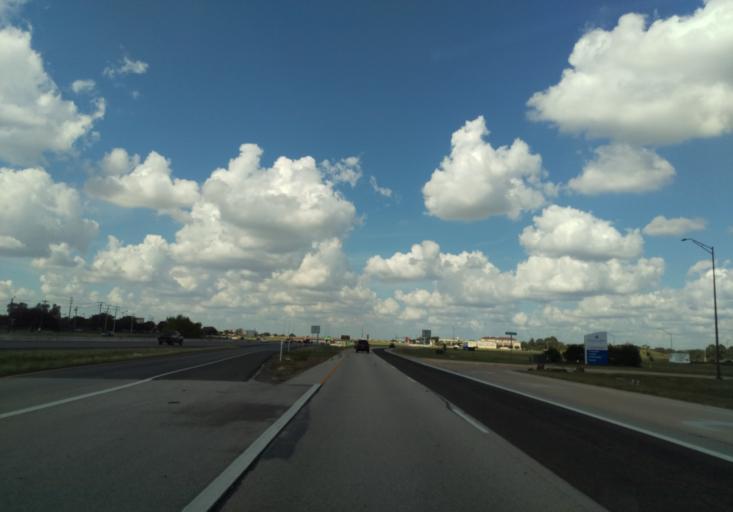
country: US
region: Texas
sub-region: Brazos County
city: College Station
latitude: 30.5799
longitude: -96.2815
